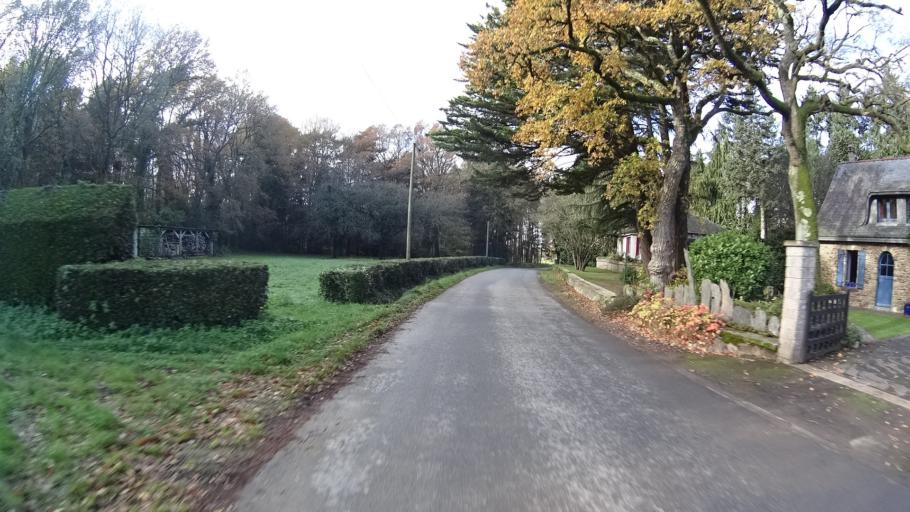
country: FR
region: Brittany
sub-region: Departement du Morbihan
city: Carentoir
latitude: 47.8237
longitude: -2.0969
